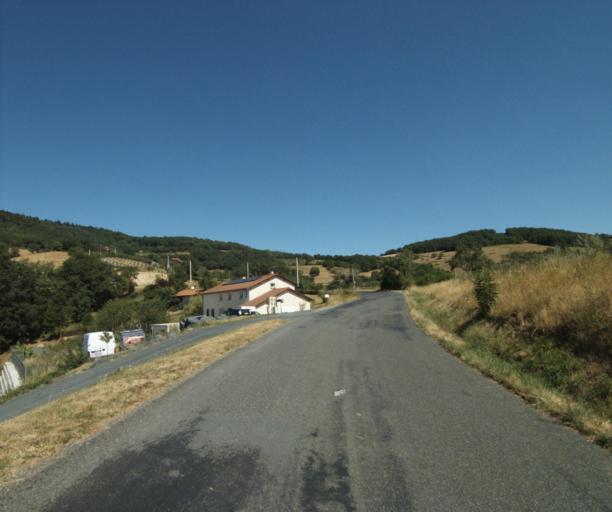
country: FR
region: Rhone-Alpes
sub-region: Departement du Rhone
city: Bessenay
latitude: 45.8009
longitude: 4.5157
